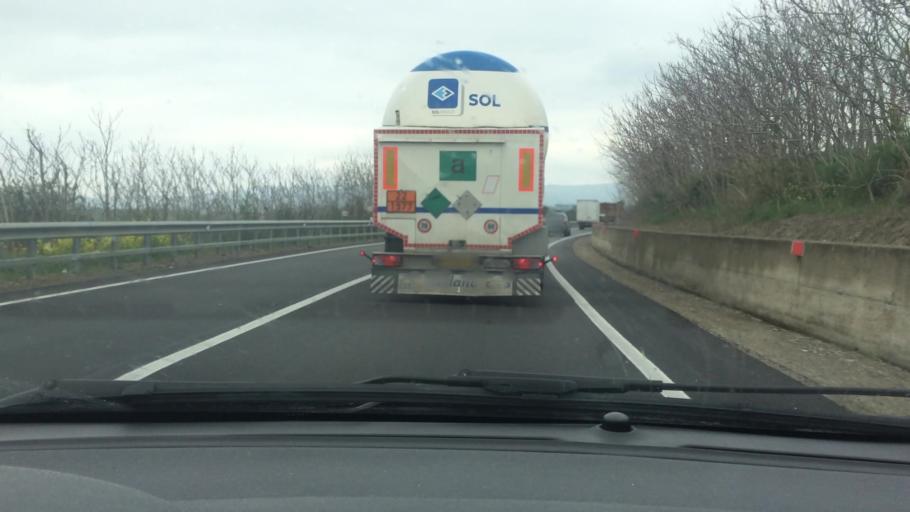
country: IT
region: Basilicate
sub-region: Provincia di Matera
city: Matera
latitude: 40.6190
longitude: 16.5827
